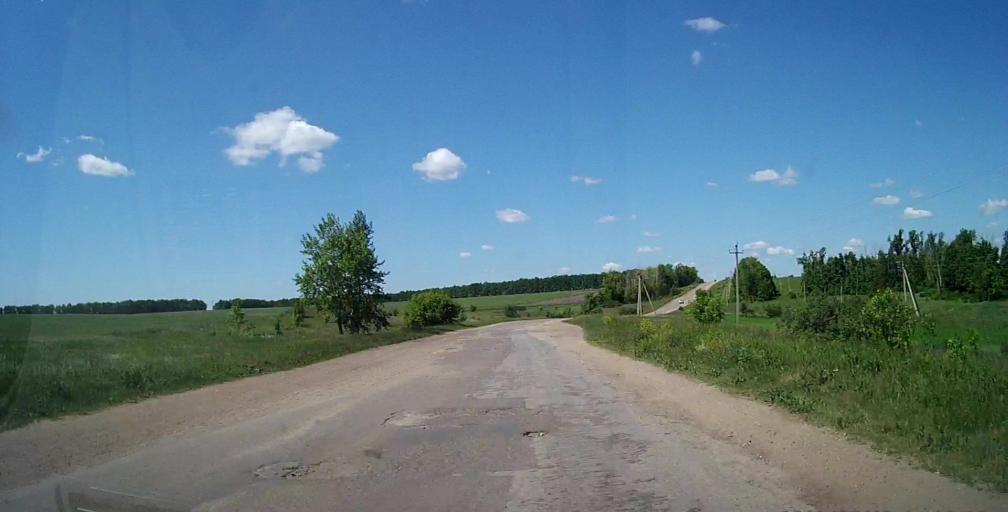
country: RU
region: Tula
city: Kurkino
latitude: 53.1847
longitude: 38.4942
